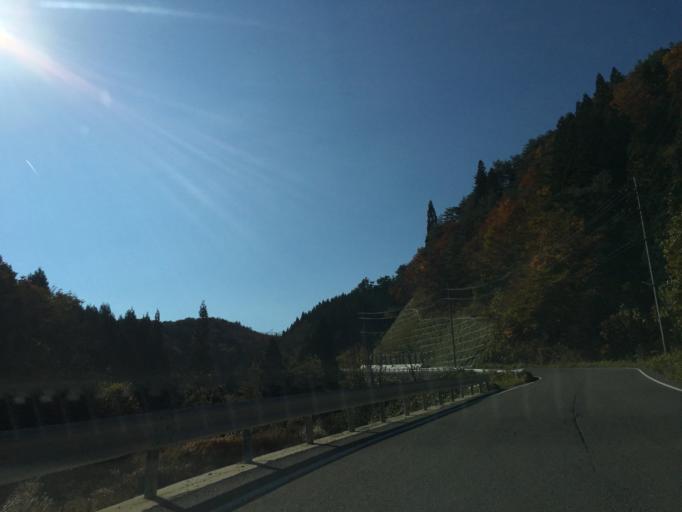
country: JP
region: Fukushima
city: Inawashiro
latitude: 37.4038
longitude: 140.1059
